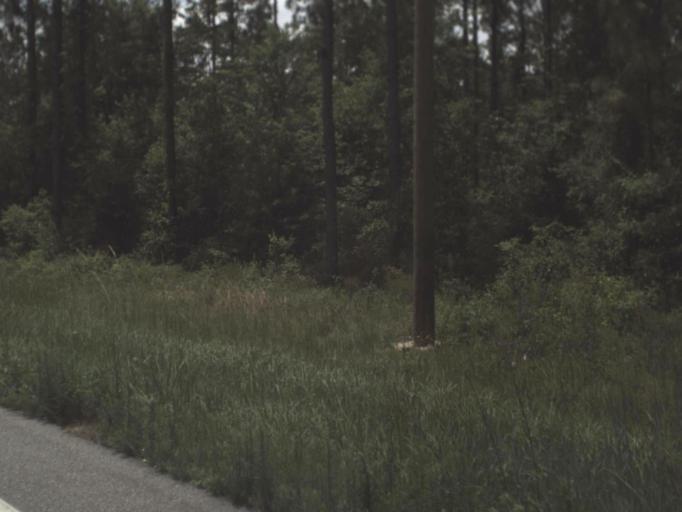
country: US
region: Florida
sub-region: Madison County
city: Madison
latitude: 30.4258
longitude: -83.3087
